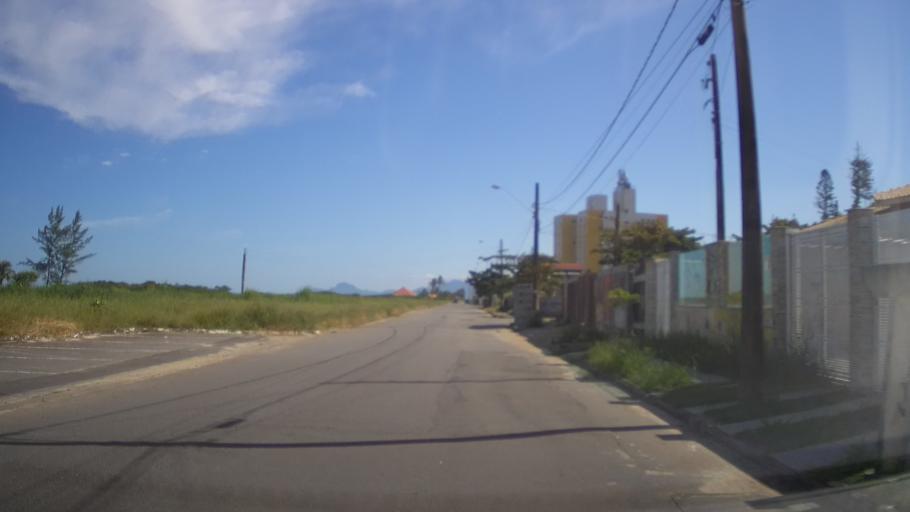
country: BR
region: Sao Paulo
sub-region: Itanhaem
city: Itanhaem
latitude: -24.2128
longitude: -46.8392
